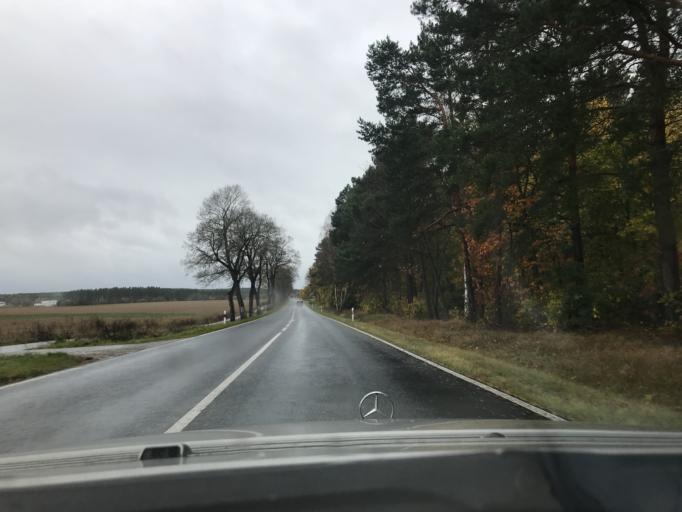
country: DE
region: Brandenburg
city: Trebbin
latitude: 52.2159
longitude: 13.1633
